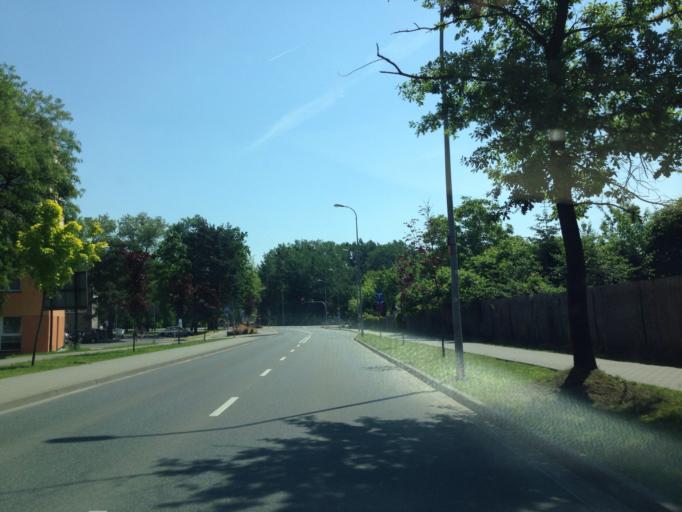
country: PL
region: Masovian Voivodeship
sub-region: Warszawa
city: Bemowo
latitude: 52.2496
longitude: 20.8959
